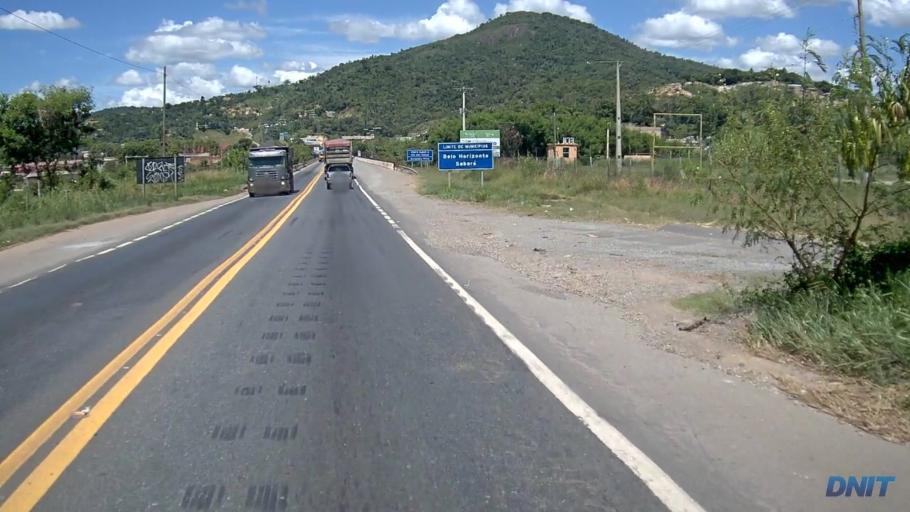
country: BR
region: Minas Gerais
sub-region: Santa Luzia
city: Santa Luzia
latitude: -19.8414
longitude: -43.8704
